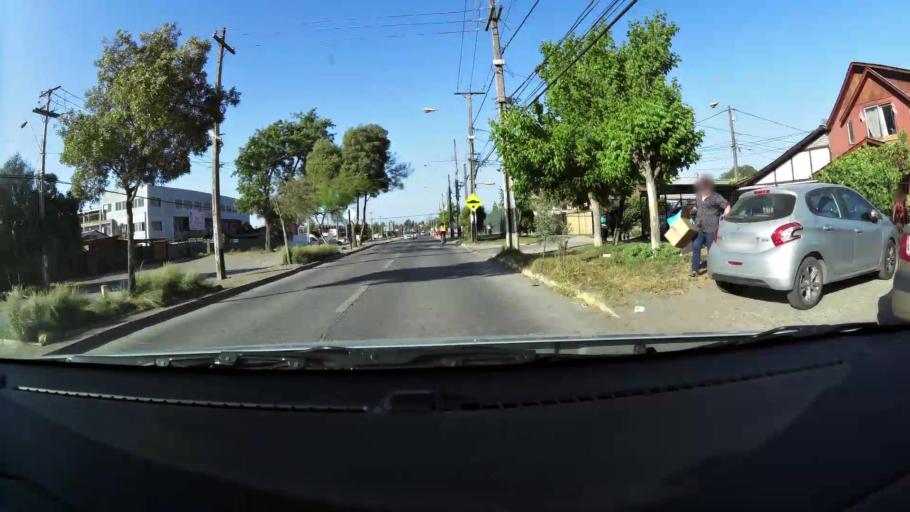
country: CL
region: Santiago Metropolitan
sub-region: Provincia de Maipo
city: San Bernardo
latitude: -33.5428
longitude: -70.7722
